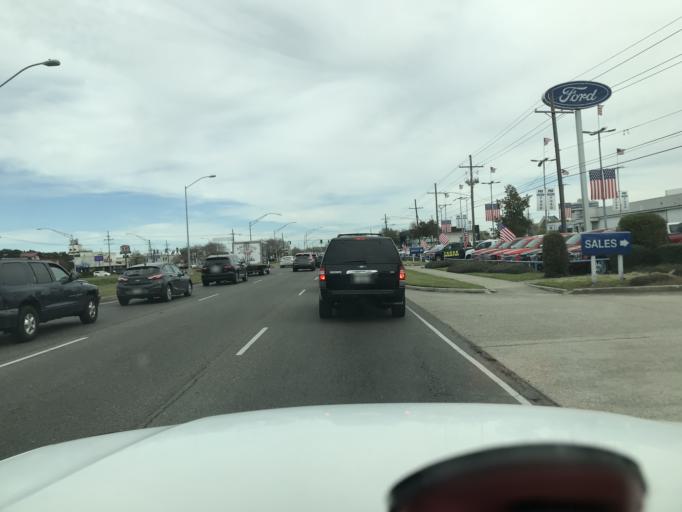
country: US
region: Louisiana
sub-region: Jefferson Parish
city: Metairie
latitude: 30.0037
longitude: -90.1665
